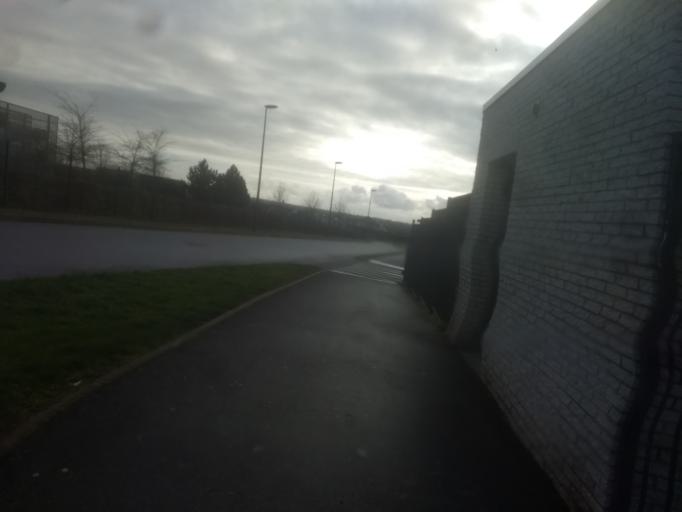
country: FR
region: Nord-Pas-de-Calais
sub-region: Departement du Pas-de-Calais
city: Dainville
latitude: 50.2917
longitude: 2.7319
